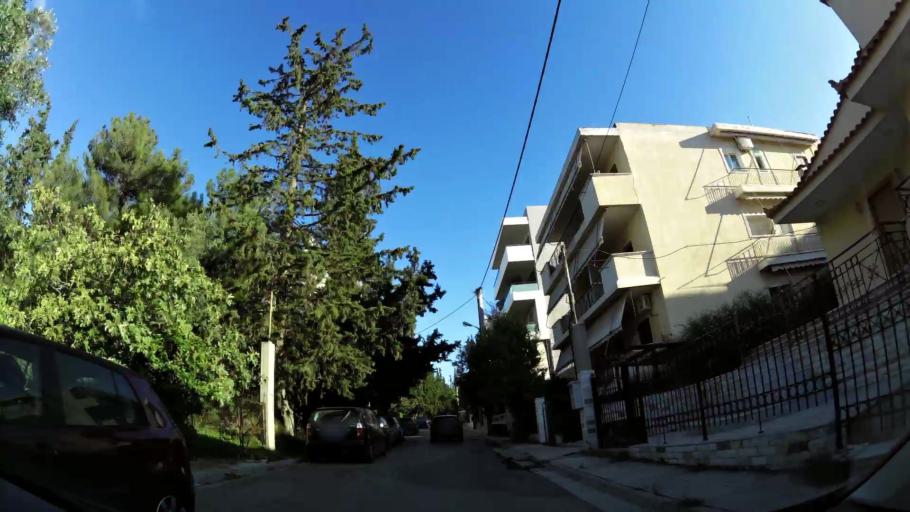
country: GR
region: Attica
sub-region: Nomarchia Anatolikis Attikis
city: Pallini
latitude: 38.0009
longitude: 23.8742
